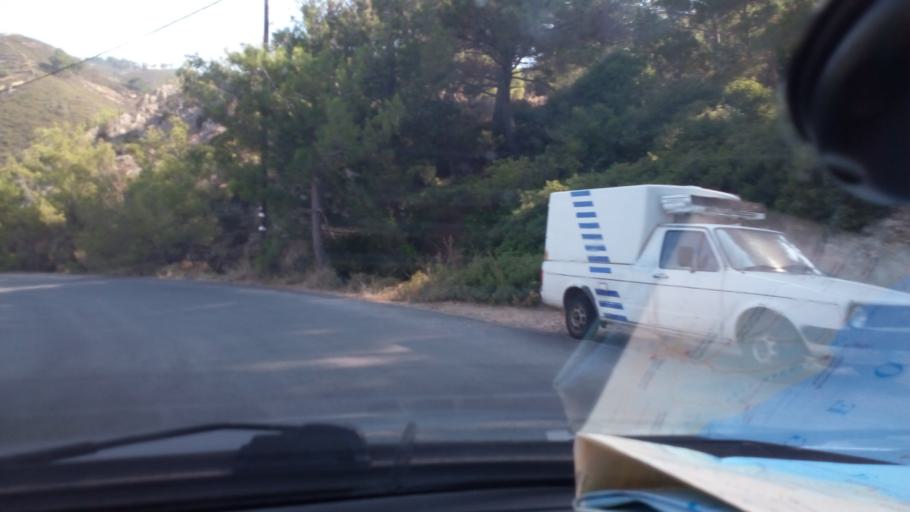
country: GR
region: North Aegean
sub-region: Nomos Samou
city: Agios Kirykos
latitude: 37.6294
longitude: 26.0889
